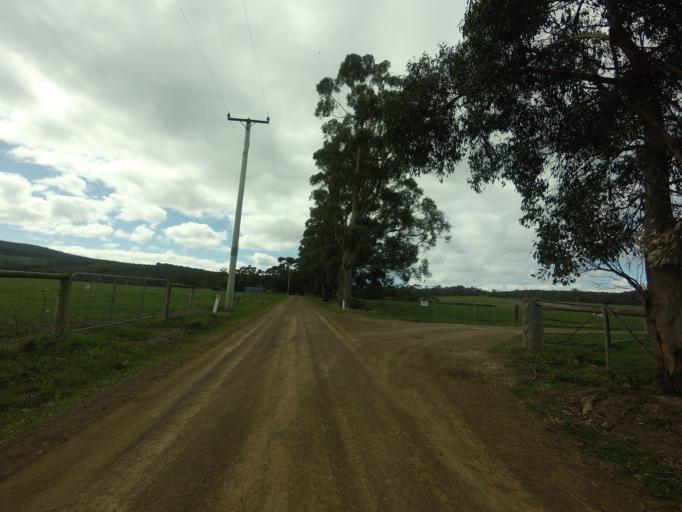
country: AU
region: Tasmania
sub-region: Huon Valley
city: Geeveston
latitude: -43.4307
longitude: 146.9909
